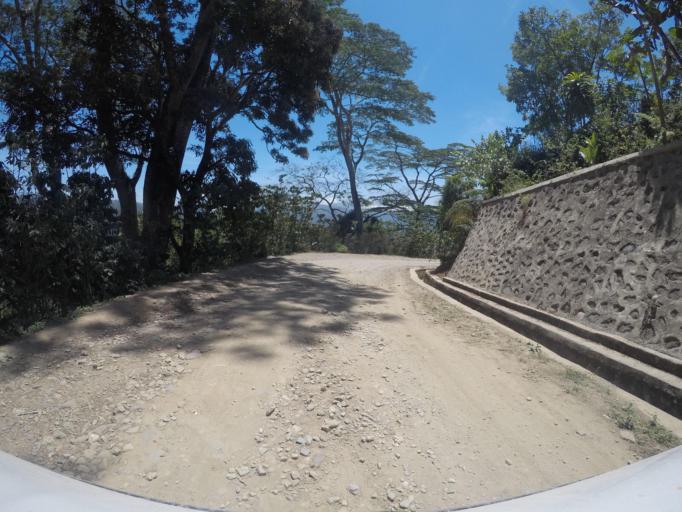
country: TL
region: Ermera
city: Gleno
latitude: -8.7432
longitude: 125.4027
